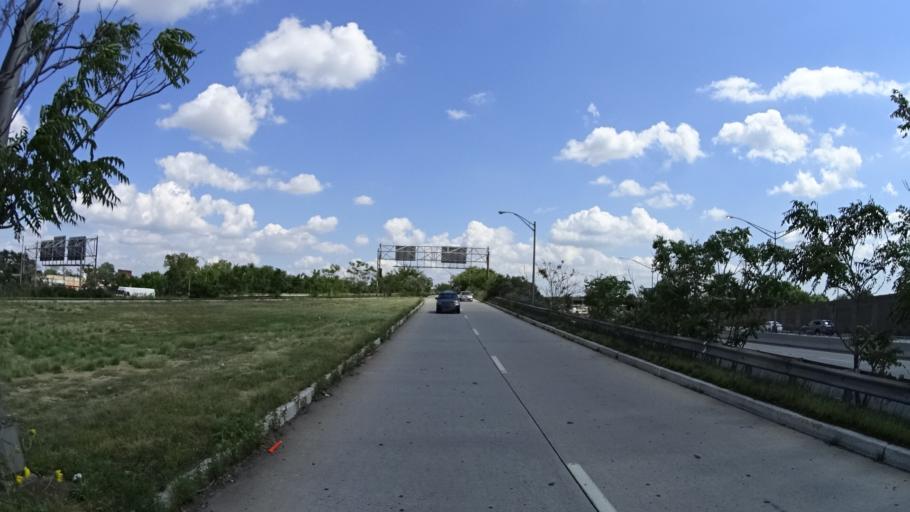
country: US
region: New Jersey
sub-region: Essex County
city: Newark
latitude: 40.7106
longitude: -74.1632
